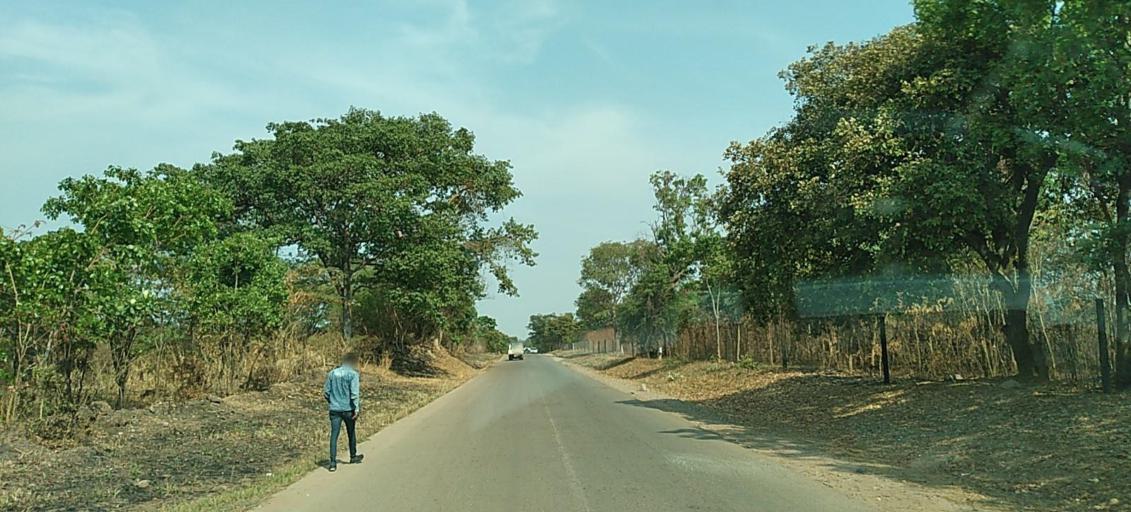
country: ZM
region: Copperbelt
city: Chililabombwe
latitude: -12.3075
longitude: 27.7907
